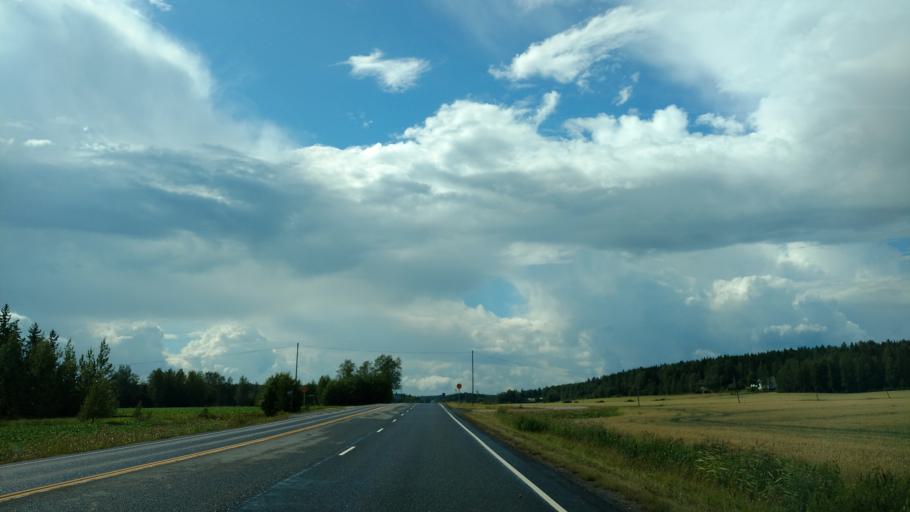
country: FI
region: Varsinais-Suomi
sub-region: Salo
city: Halikko
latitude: 60.3760
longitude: 22.9707
